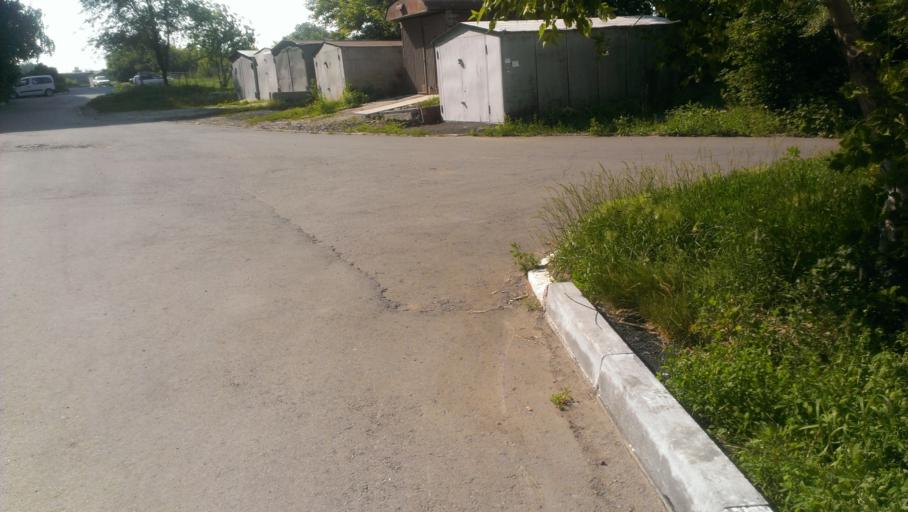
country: RU
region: Altai Krai
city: Novosilikatnyy
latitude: 53.3833
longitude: 83.6736
